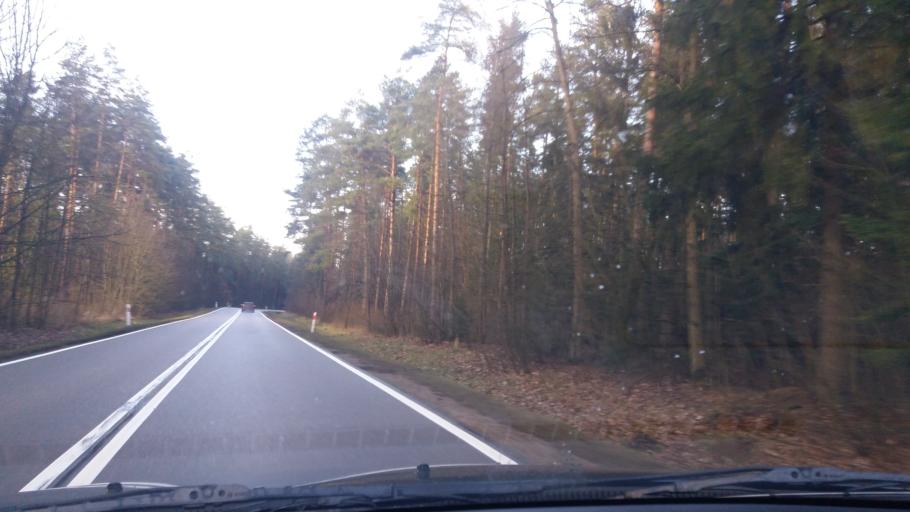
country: PL
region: Warmian-Masurian Voivodeship
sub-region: Powiat szczycienski
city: Wielbark
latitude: 53.4393
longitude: 20.9465
